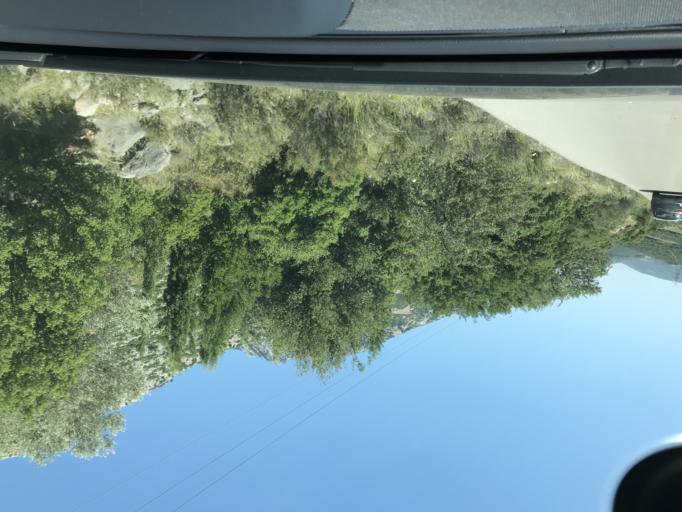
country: GR
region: Central Greece
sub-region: Nomos Voiotias
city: Distomo
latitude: 38.4843
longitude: 22.6882
